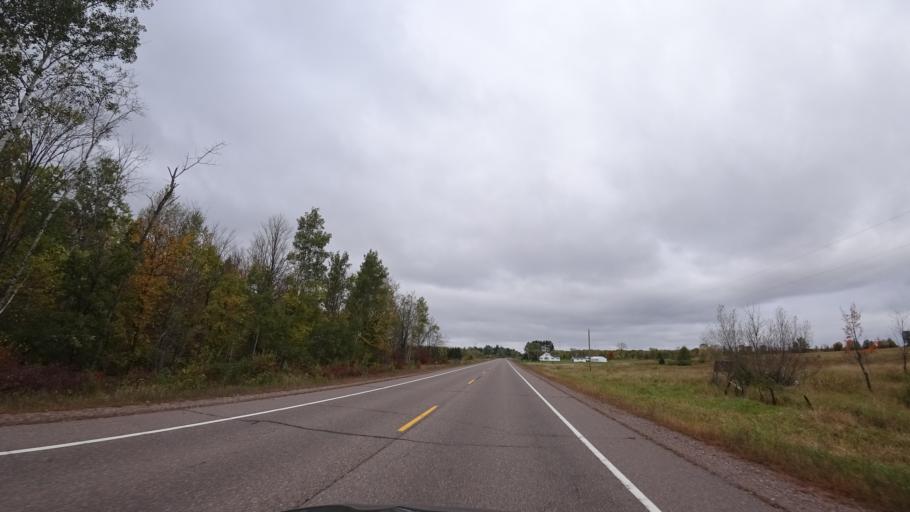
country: US
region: Wisconsin
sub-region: Rusk County
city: Ladysmith
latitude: 45.5471
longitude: -91.1117
